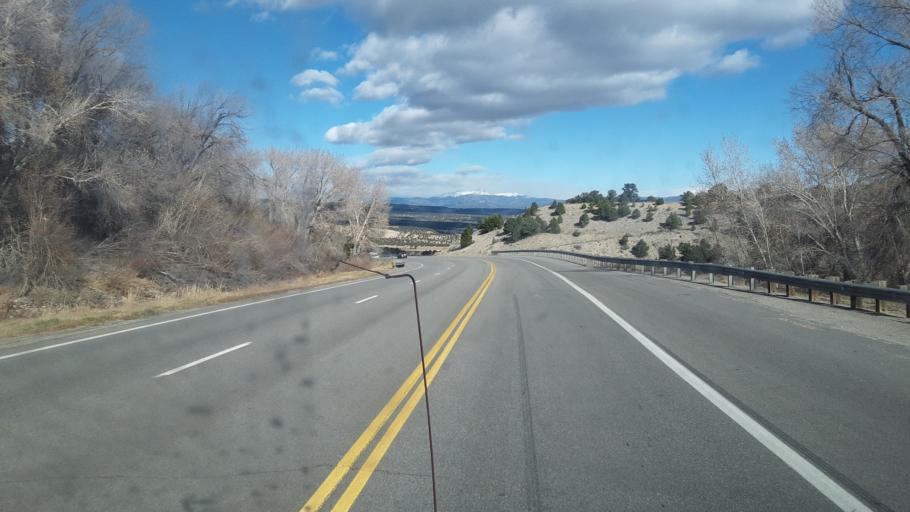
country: US
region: Colorado
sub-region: Chaffee County
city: Salida
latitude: 38.5482
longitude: -106.0796
